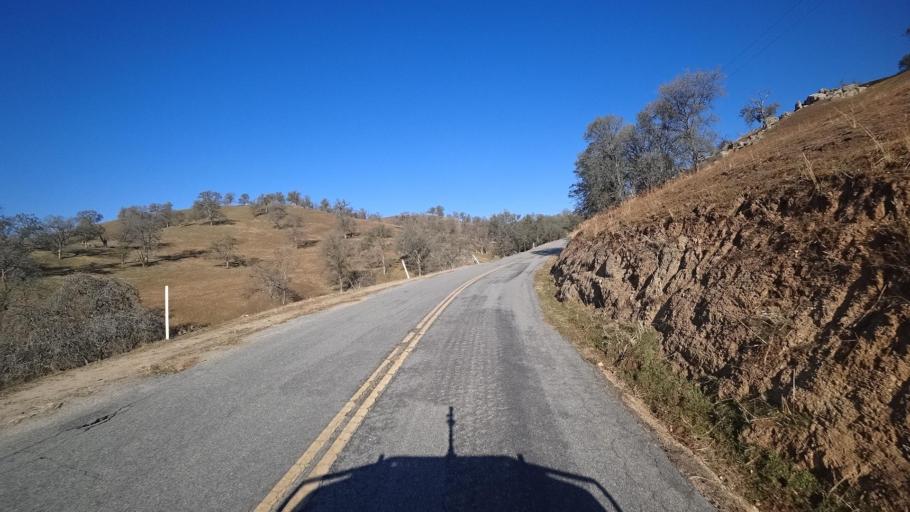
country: US
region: California
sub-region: Kern County
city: Alta Sierra
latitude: 35.7295
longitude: -118.8129
